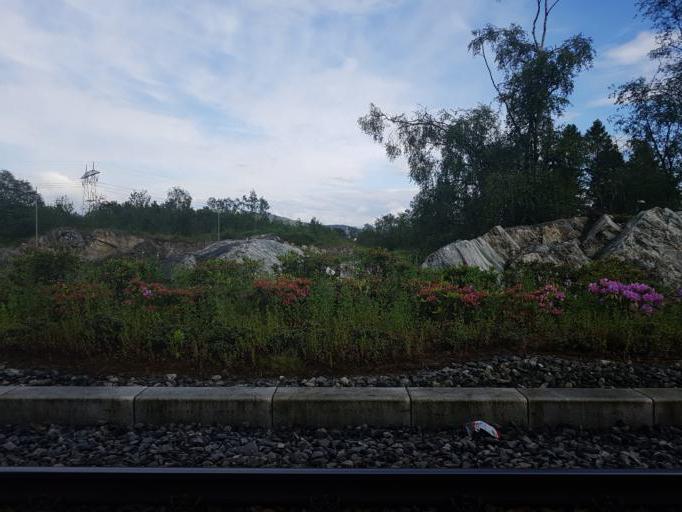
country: NO
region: Hordaland
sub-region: Bergen
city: Ytrebygda
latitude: 60.2935
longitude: 5.2677
